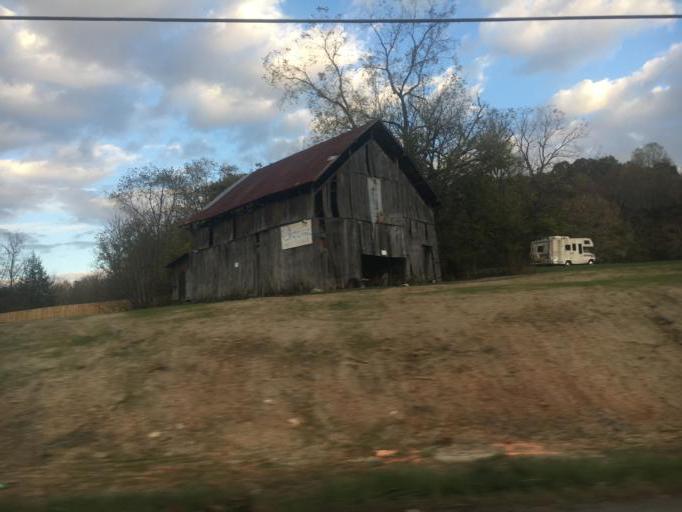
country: US
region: Tennessee
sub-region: Sullivan County
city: Colonial Heights
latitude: 36.4686
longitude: -82.4840
